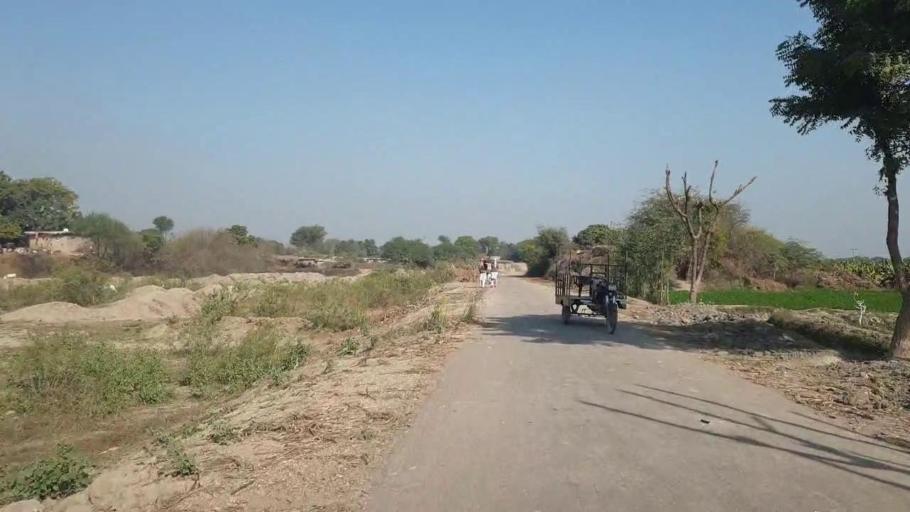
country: PK
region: Sindh
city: Tando Jam
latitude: 25.3773
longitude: 68.6379
